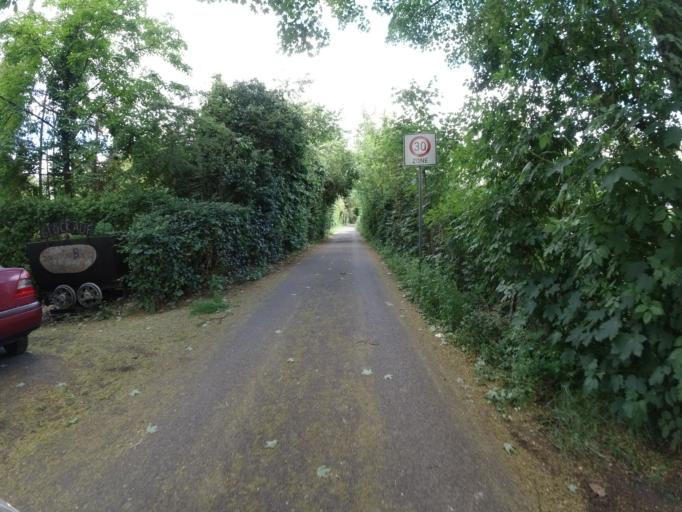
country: DE
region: North Rhine-Westphalia
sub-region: Regierungsbezirk Dusseldorf
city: Hochfeld
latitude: 51.3945
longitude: 6.6944
